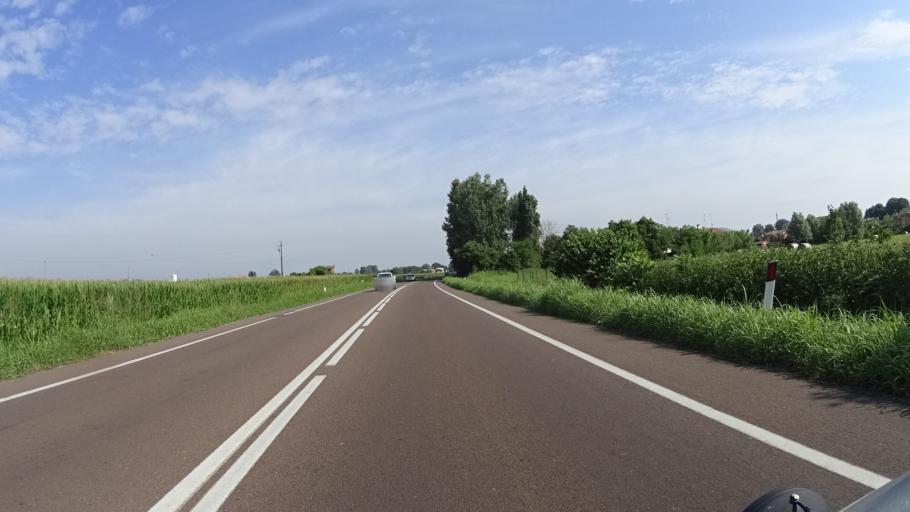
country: IT
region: Veneto
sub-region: Provincia di Venezia
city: San Michele al Tagliamento
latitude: 45.7611
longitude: 12.9860
